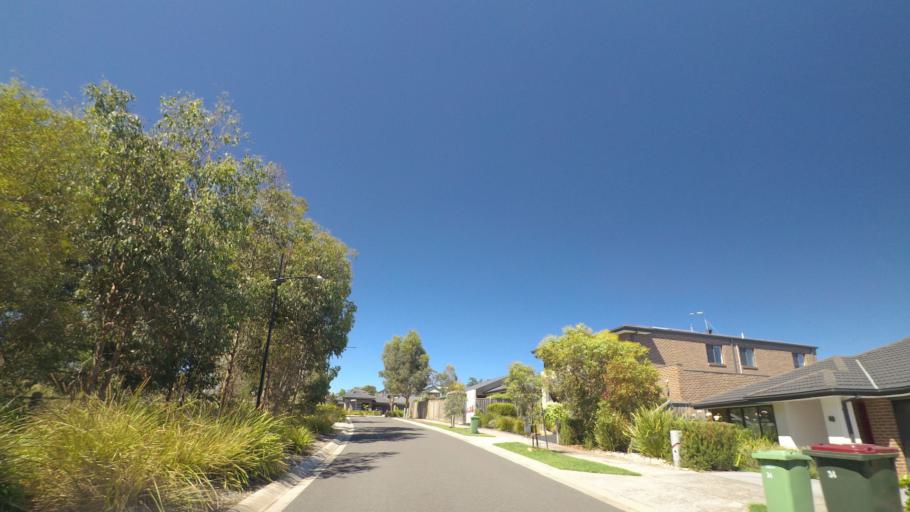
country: AU
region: Victoria
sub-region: Maroondah
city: Croydon North
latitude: -37.7787
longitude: 145.2959
